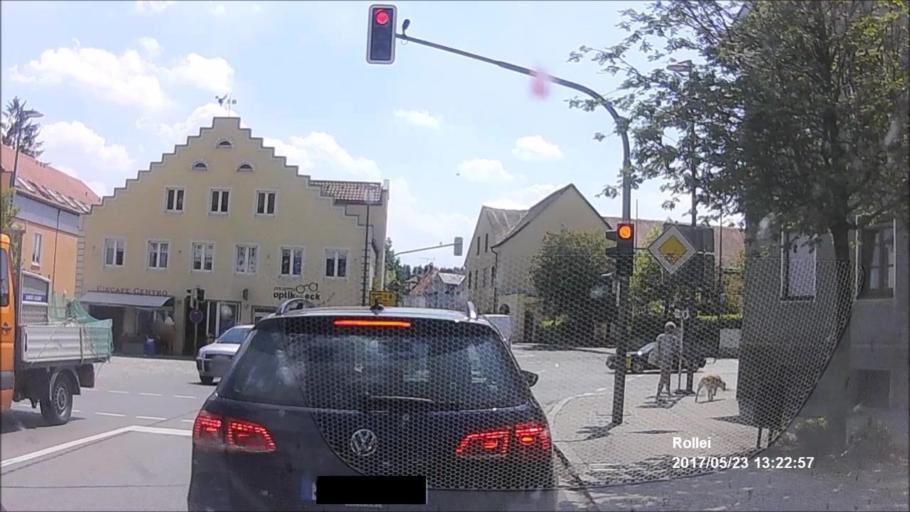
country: DE
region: Bavaria
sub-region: Upper Bavaria
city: Taufkirchen
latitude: 48.3437
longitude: 12.1308
